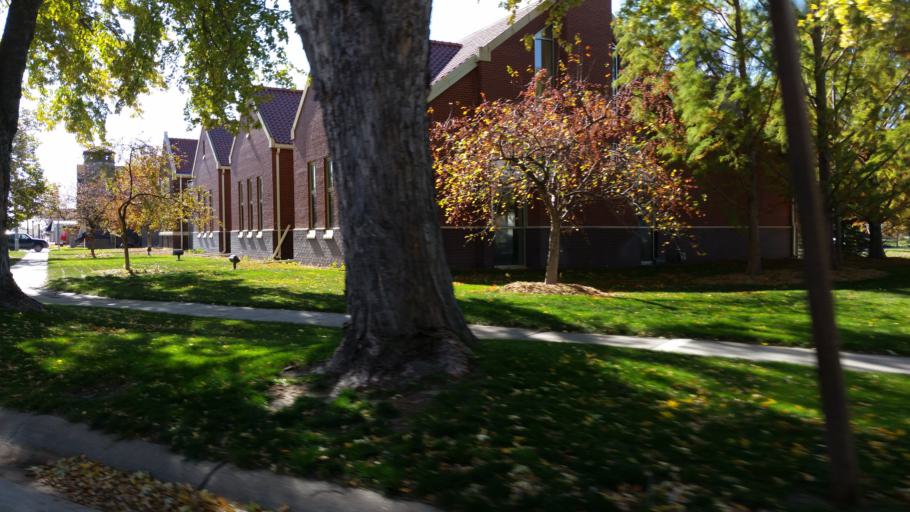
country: US
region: Nebraska
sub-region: Dawson County
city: Gothenburg
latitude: 40.9302
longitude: -100.1603
